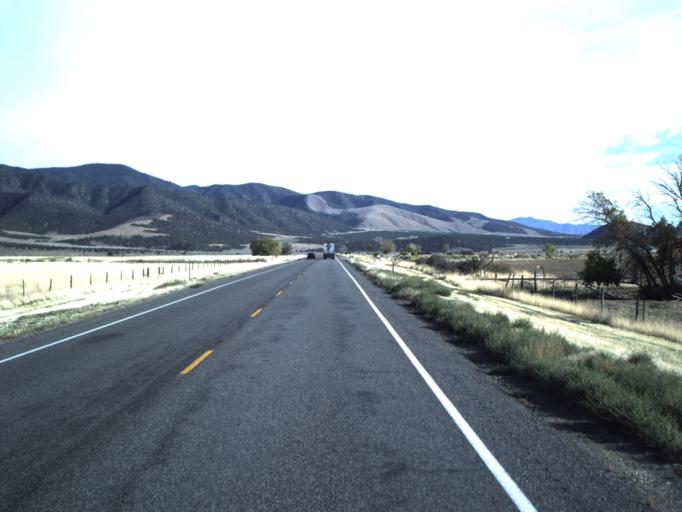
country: US
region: Utah
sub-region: Sanpete County
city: Gunnison
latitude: 39.2337
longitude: -112.1003
